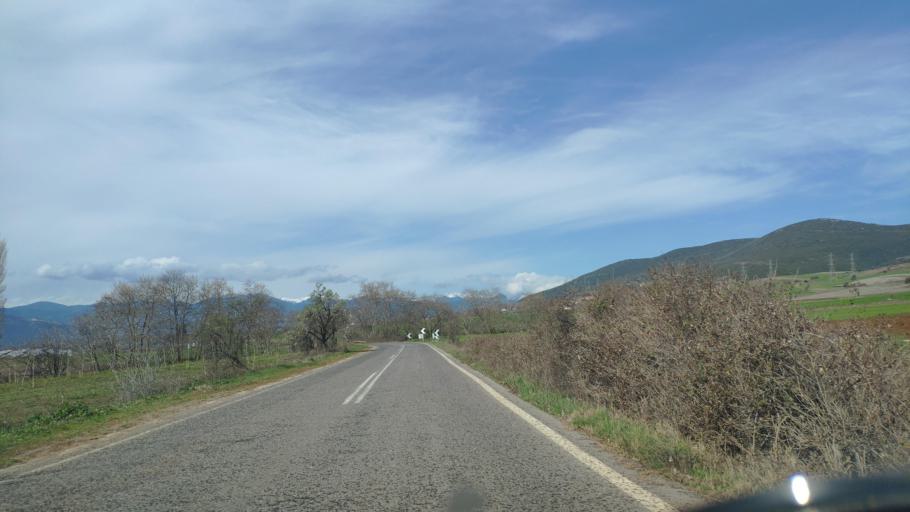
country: GR
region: Central Greece
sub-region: Nomos Fthiotidos
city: Amfikleia
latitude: 38.7055
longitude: 22.5035
